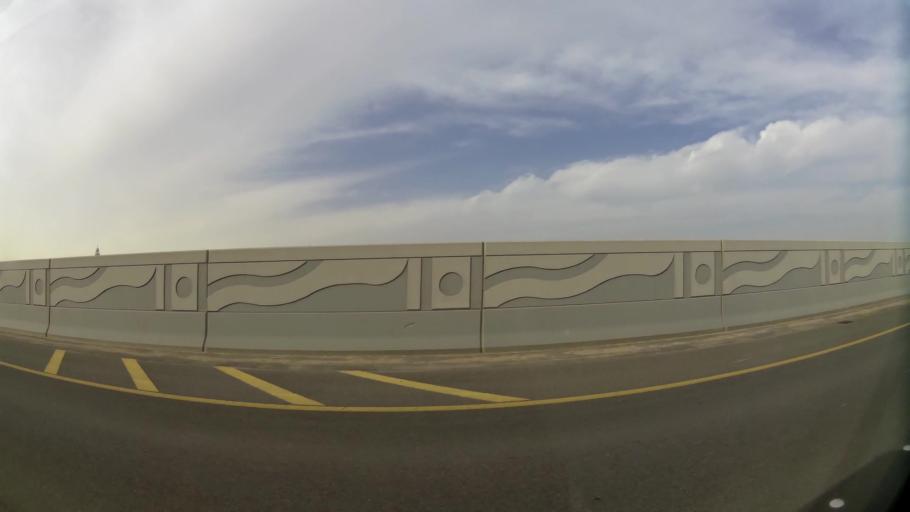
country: QA
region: Baladiyat ad Dawhah
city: Doha
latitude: 25.2547
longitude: 51.5074
